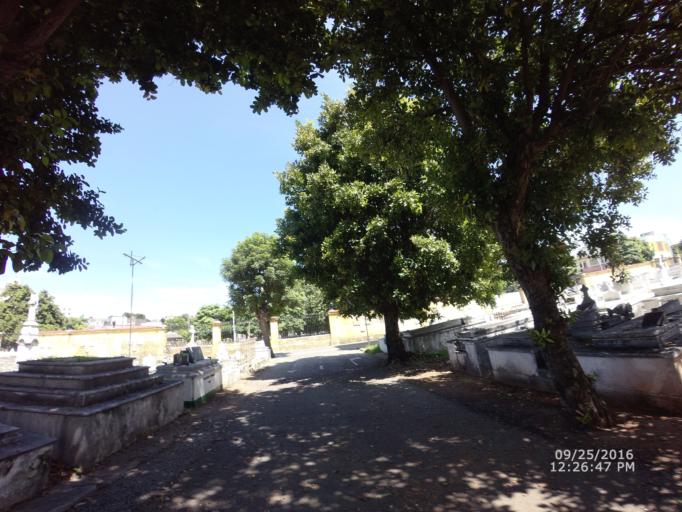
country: CU
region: La Habana
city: Havana
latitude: 23.1256
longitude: -82.3972
